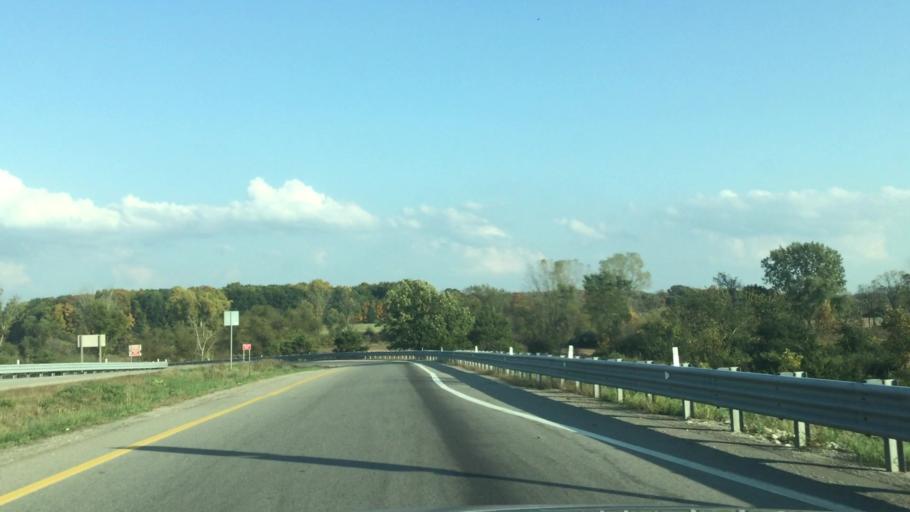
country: US
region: Michigan
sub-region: Washtenaw County
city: Chelsea
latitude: 42.2928
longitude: -84.0276
